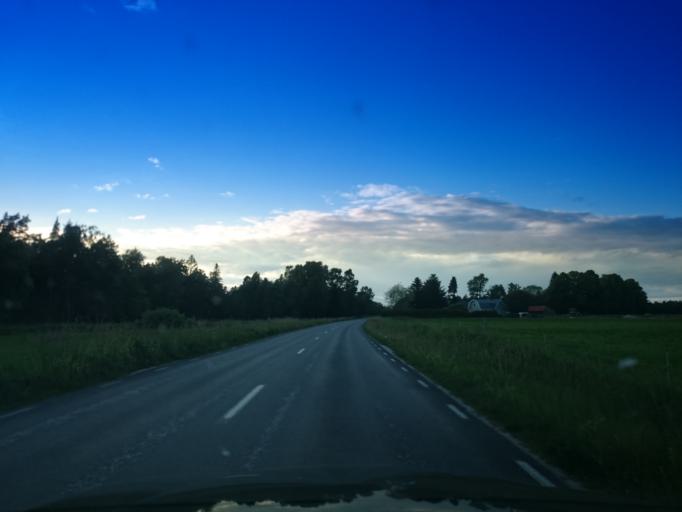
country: SE
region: Gotland
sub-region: Gotland
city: Hemse
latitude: 57.3268
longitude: 18.3814
